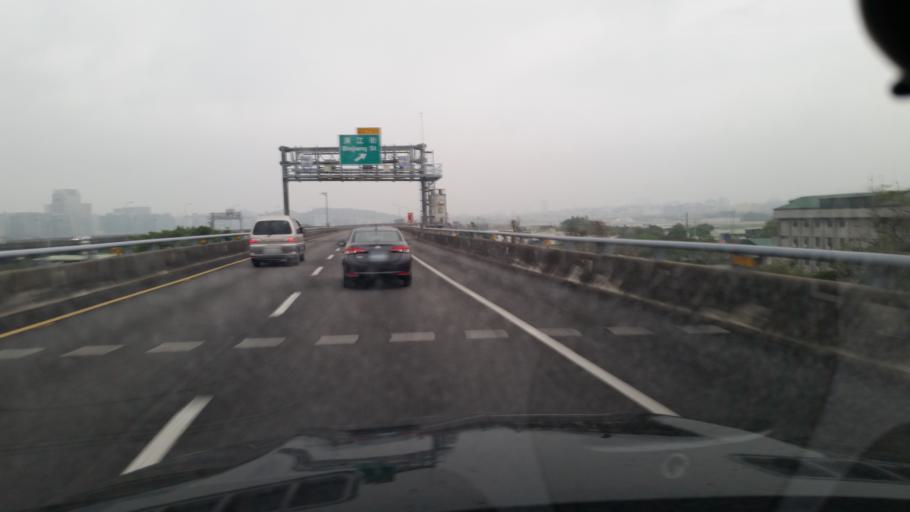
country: TW
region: Taipei
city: Taipei
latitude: 25.0722
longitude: 121.5545
